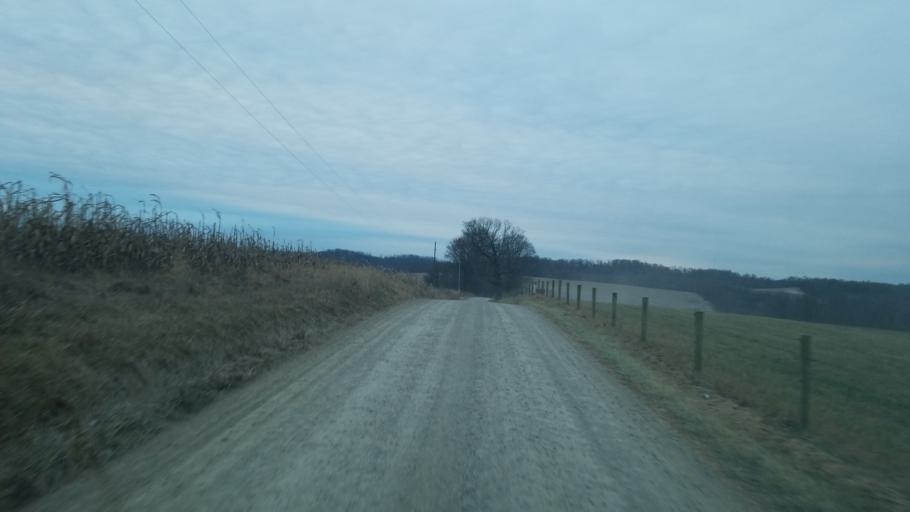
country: US
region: Ohio
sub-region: Holmes County
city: Millersburg
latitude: 40.4608
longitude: -81.8488
